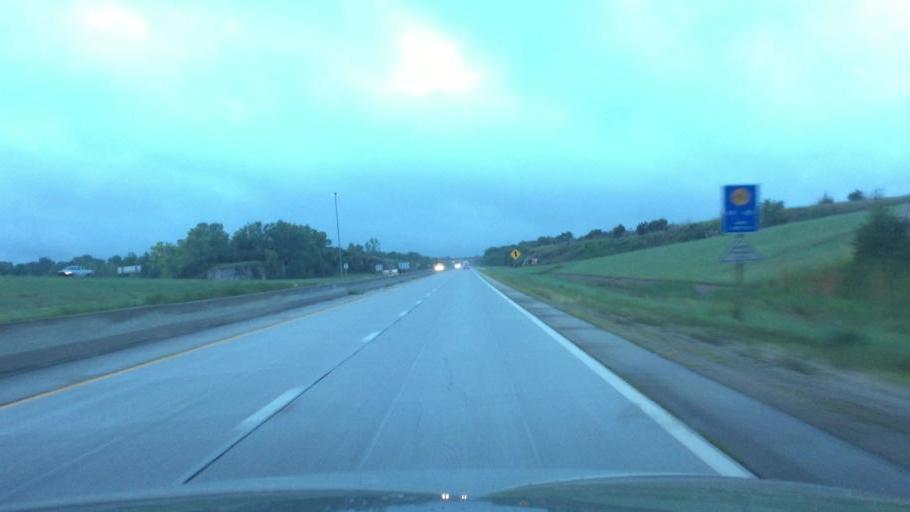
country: US
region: Kansas
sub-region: Neosho County
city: Chanute
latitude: 37.6890
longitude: -95.4796
